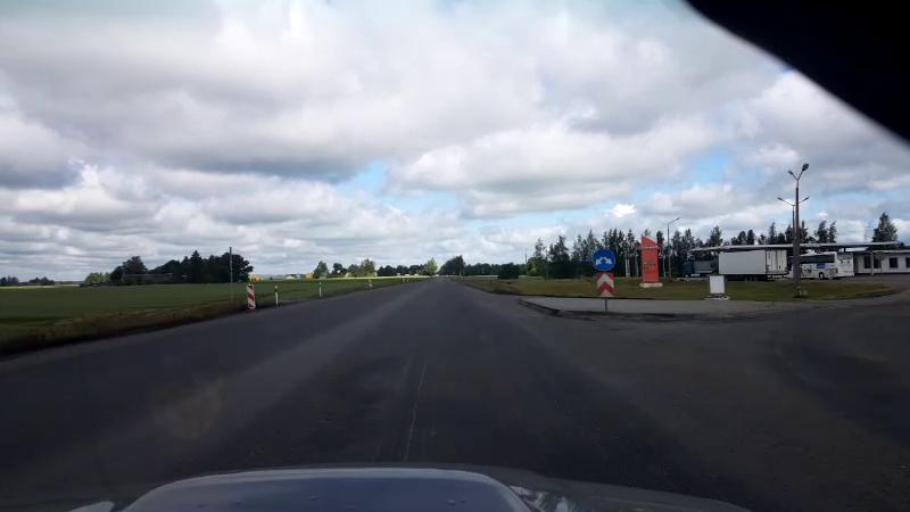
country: LV
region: Bauskas Rajons
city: Bauska
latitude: 56.3151
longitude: 24.3290
